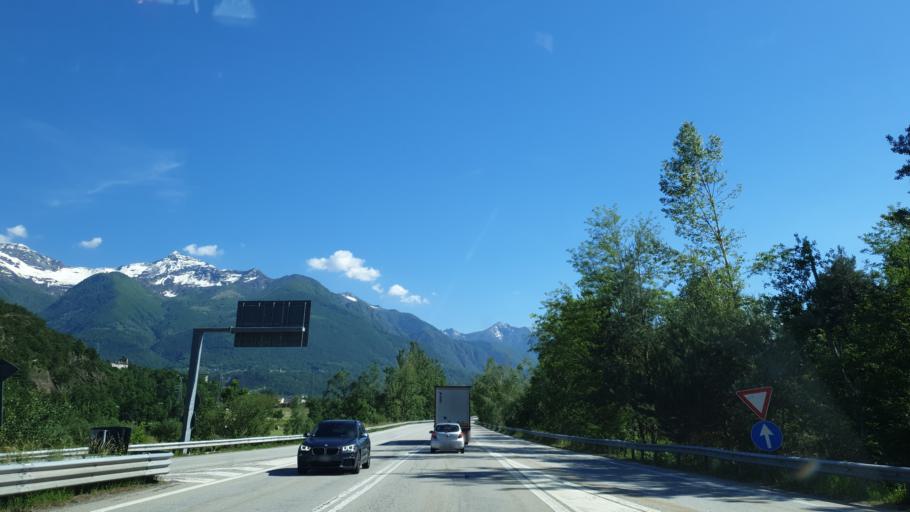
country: IT
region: Piedmont
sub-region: Provincia Verbano-Cusio-Ossola
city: Montecrestese
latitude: 46.1585
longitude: 8.3130
